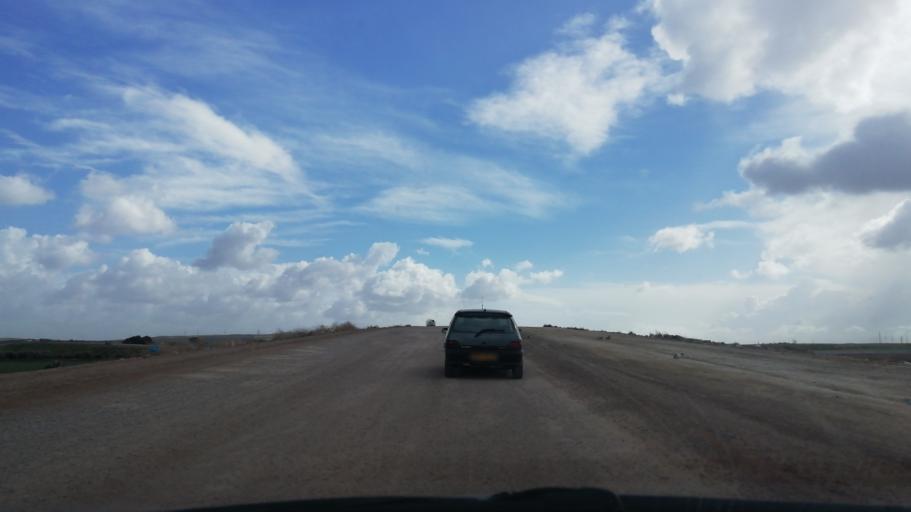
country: DZ
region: Oran
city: Sidi ech Chahmi
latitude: 35.6357
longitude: -0.5404
